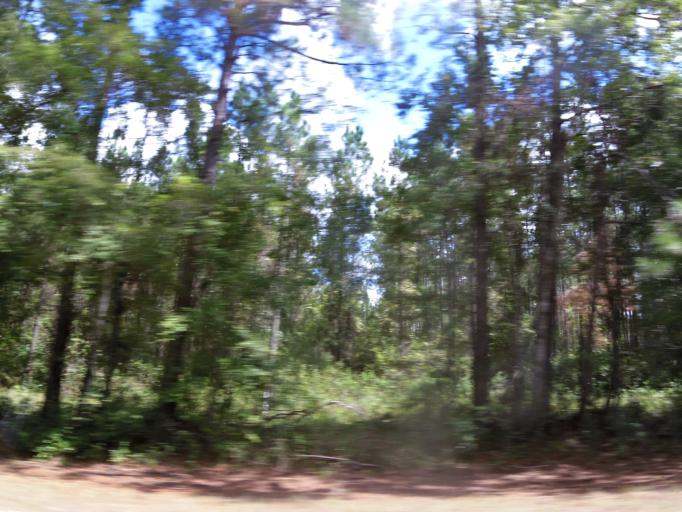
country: US
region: Georgia
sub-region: Charlton County
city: Folkston
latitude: 30.9432
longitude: -82.0226
